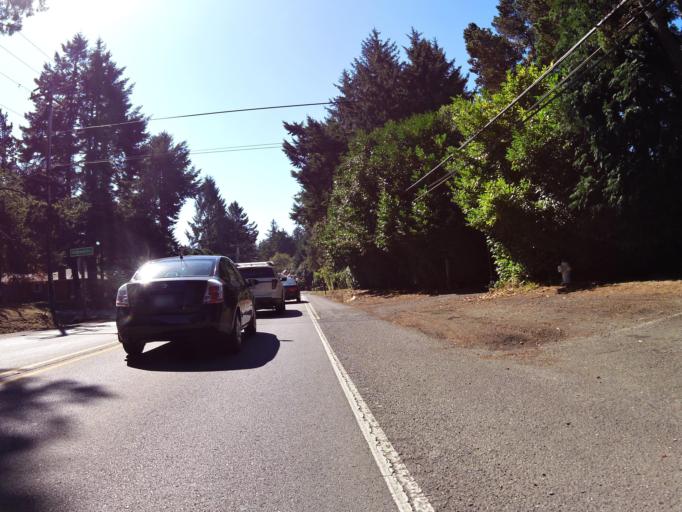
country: US
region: Oregon
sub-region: Coos County
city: Barview
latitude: 43.3484
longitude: -124.3145
